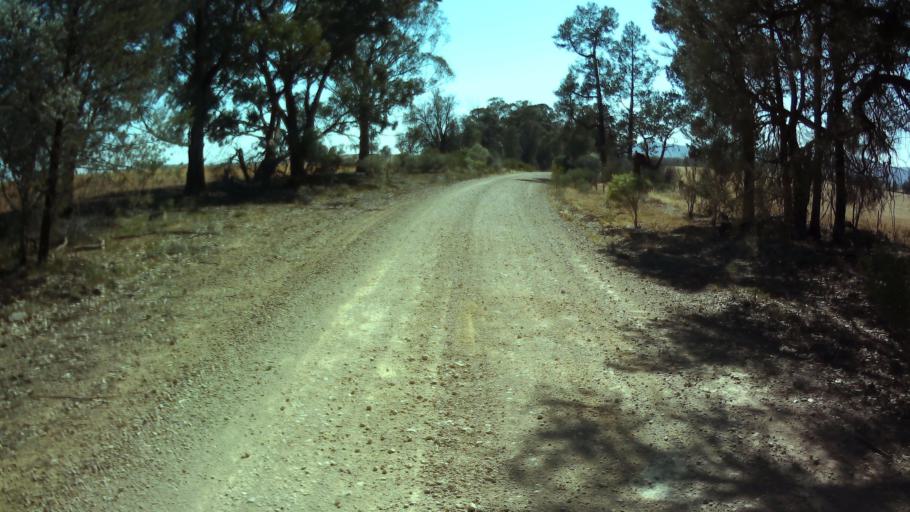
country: AU
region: New South Wales
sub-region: Weddin
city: Grenfell
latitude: -33.9044
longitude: 147.8587
